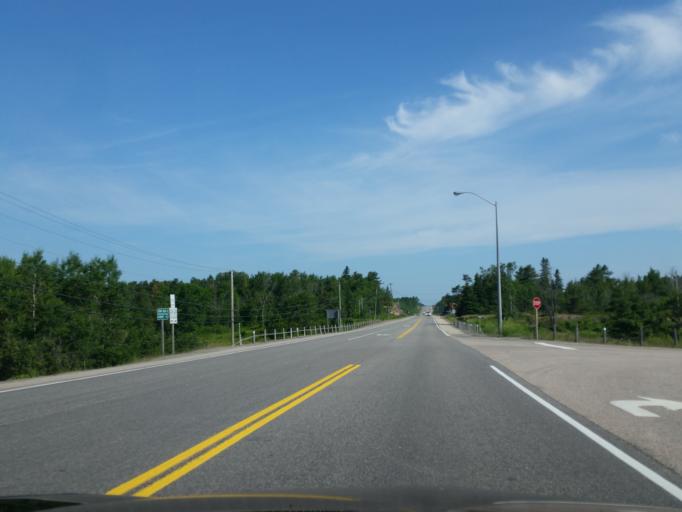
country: CA
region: Ontario
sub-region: Parry Sound District
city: Parry Sound
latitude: 45.8030
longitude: -80.5376
